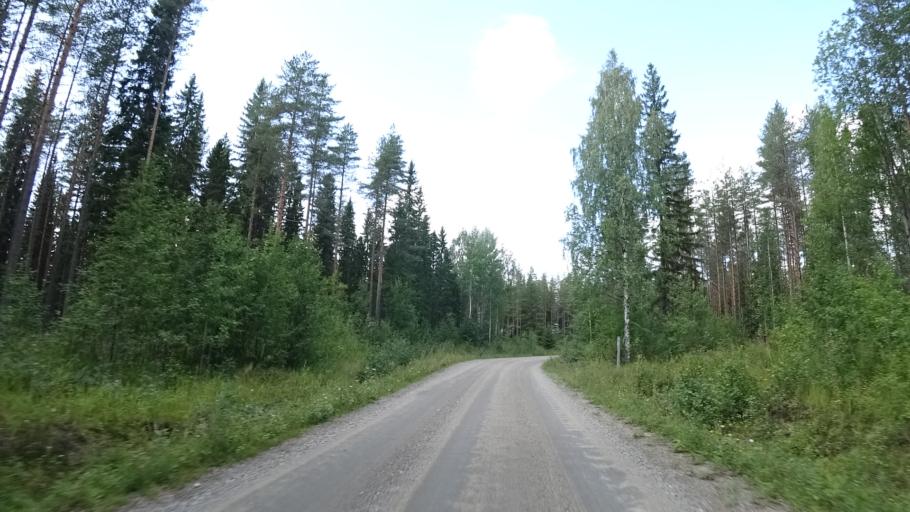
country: FI
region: North Karelia
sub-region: Joensuu
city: Ilomantsi
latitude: 62.9225
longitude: 31.3356
